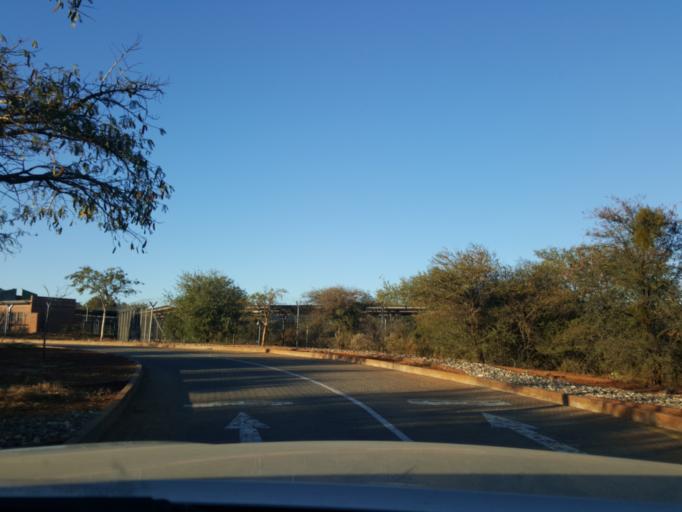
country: BW
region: South East
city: Lobatse
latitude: -25.2779
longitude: 25.7141
